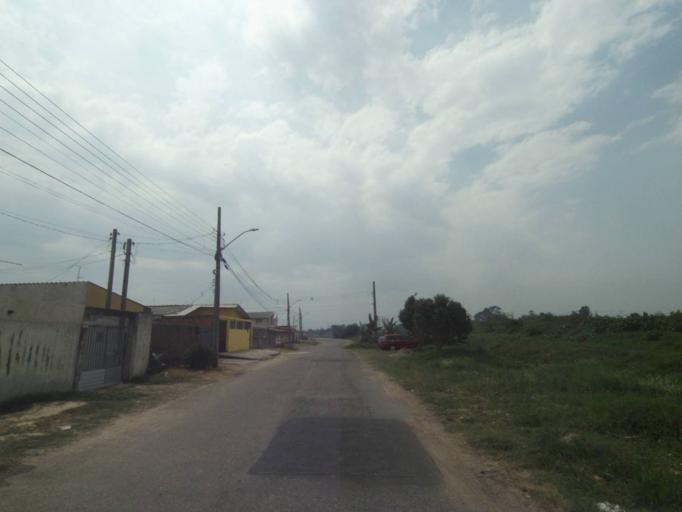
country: BR
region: Parana
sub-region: Pinhais
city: Pinhais
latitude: -25.4853
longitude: -49.1931
